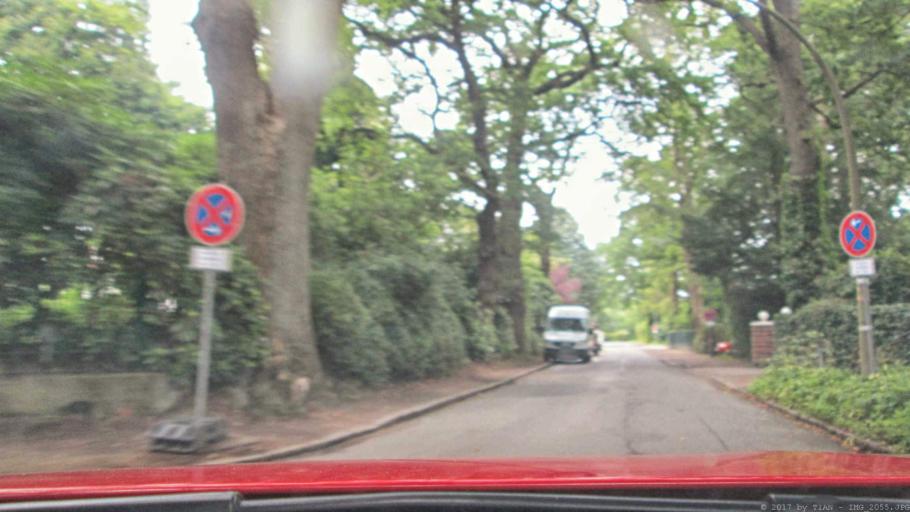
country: DE
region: Hamburg
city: Eidelstedt
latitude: 53.5584
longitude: 9.8561
